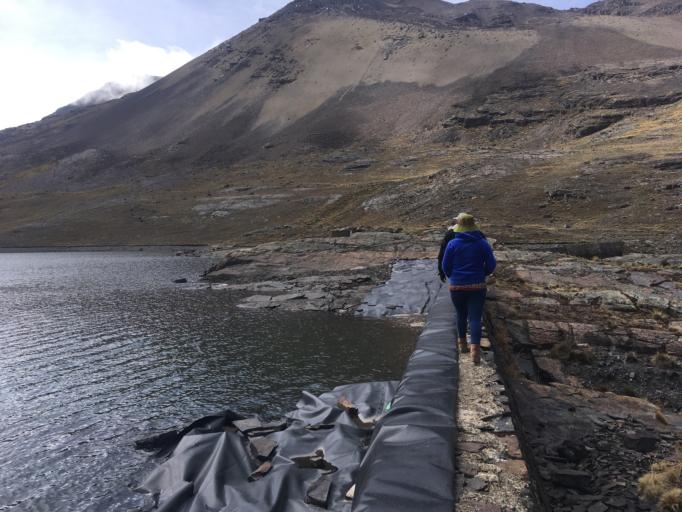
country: BO
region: La Paz
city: La Paz
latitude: -16.3963
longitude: -67.9707
